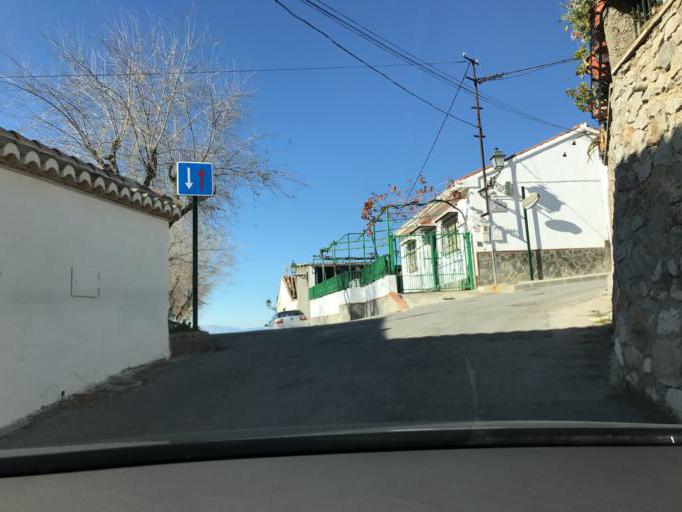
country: ES
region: Andalusia
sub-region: Provincia de Granada
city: Viznar
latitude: 37.2087
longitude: -3.5582
